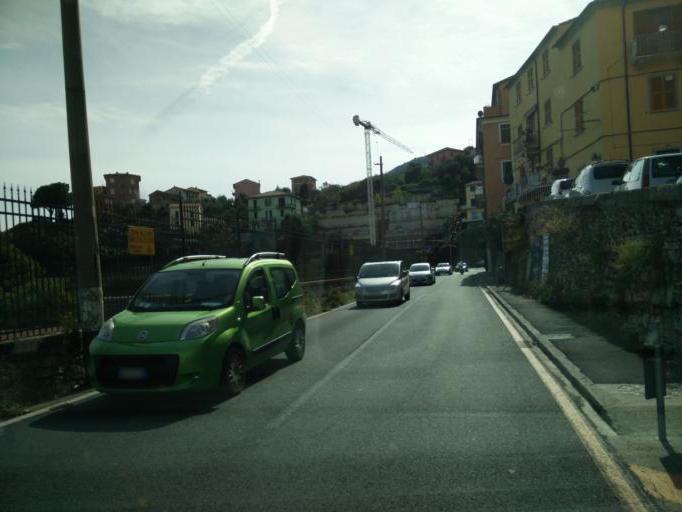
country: IT
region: Liguria
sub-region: Provincia di La Spezia
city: Le Grazie
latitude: 44.0876
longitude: 9.8201
